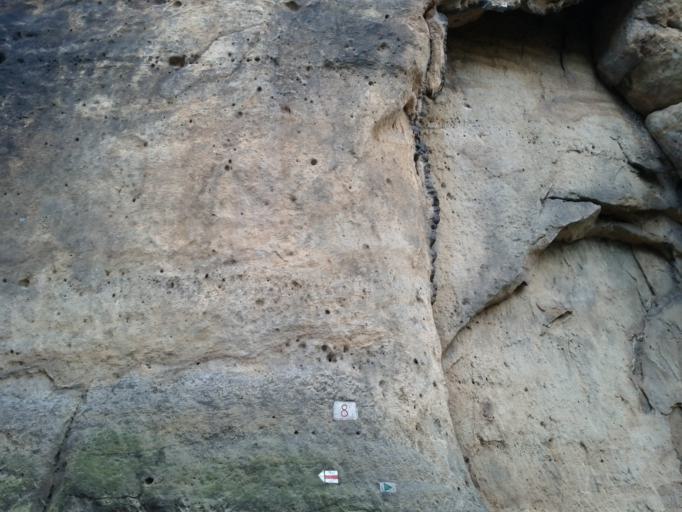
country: DE
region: Saxony
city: Sebnitz
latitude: 50.9202
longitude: 14.2356
